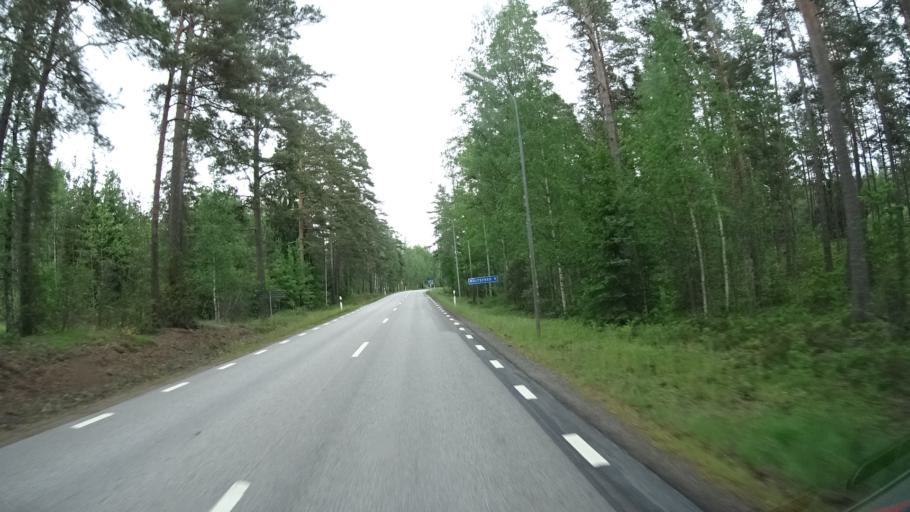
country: SE
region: Kalmar
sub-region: Hultsfreds Kommun
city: Hultsfred
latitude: 57.5343
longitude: 15.7673
